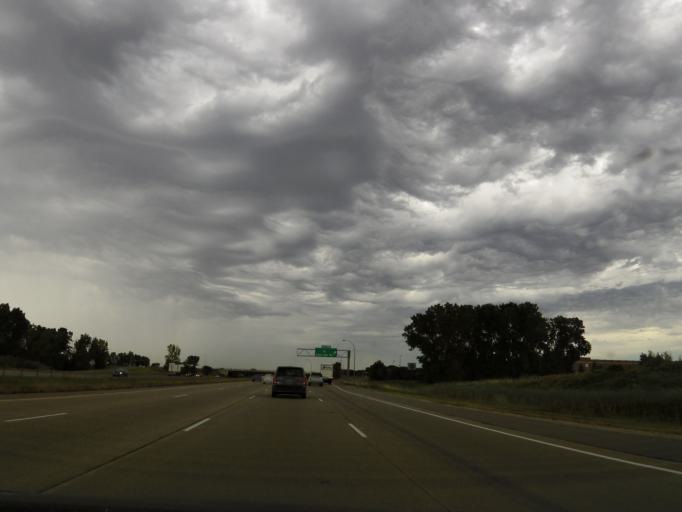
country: US
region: Minnesota
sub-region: Dakota County
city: Eagan
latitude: 44.8435
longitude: -93.1562
